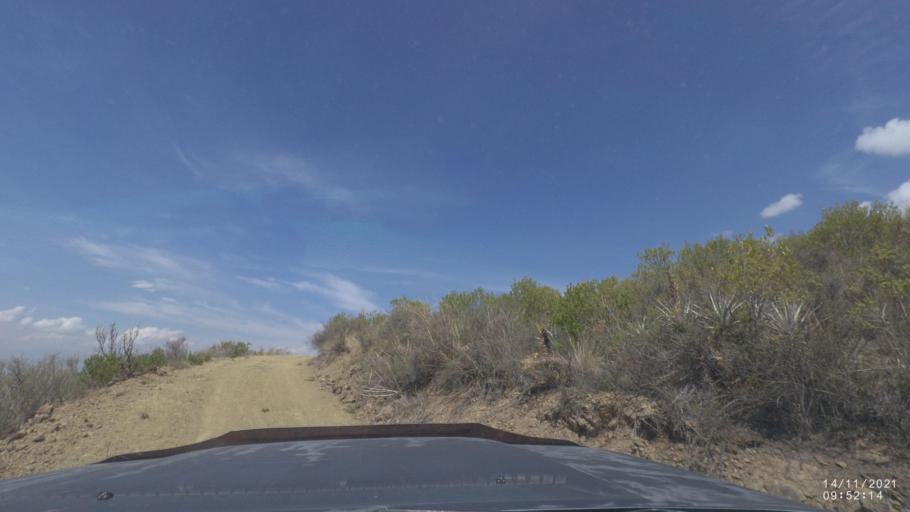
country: BO
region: Cochabamba
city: Cochabamba
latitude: -17.3613
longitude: -66.0879
